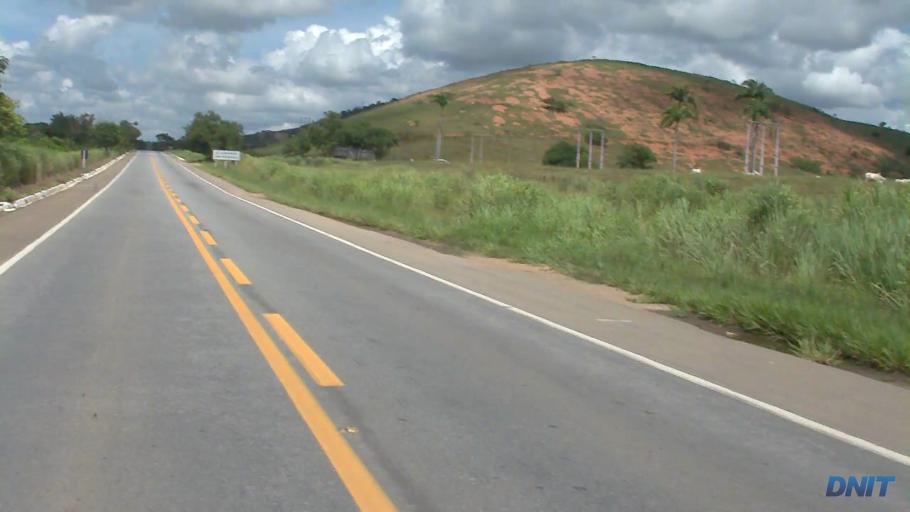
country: BR
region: Minas Gerais
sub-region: Governador Valadares
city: Governador Valadares
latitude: -18.9432
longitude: -42.0620
